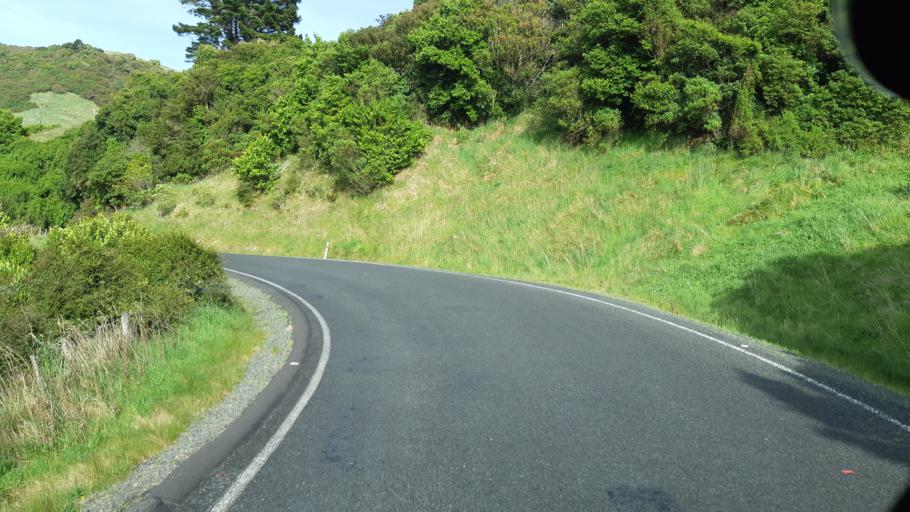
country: NZ
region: Otago
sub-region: Dunedin City
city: Portobello
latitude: -45.8661
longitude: 170.6367
